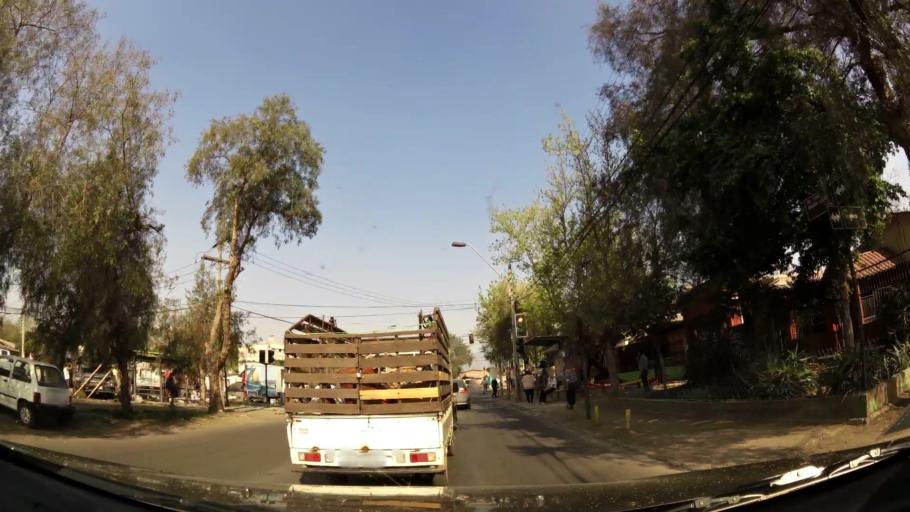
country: CL
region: Santiago Metropolitan
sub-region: Provincia de Santiago
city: Santiago
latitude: -33.3830
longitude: -70.6681
